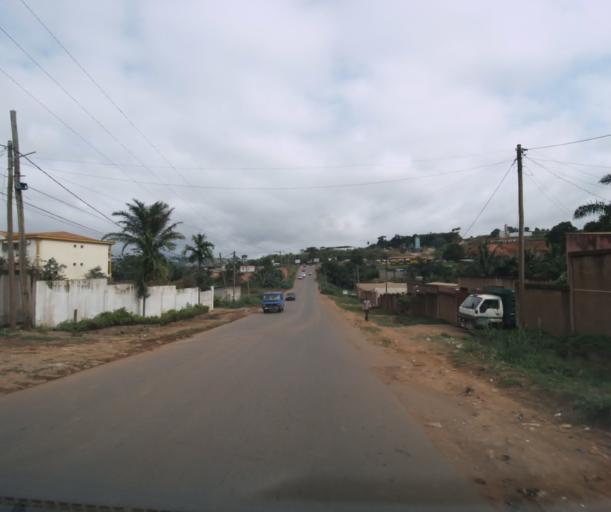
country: CM
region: Centre
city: Yaounde
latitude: 3.8059
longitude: 11.5207
